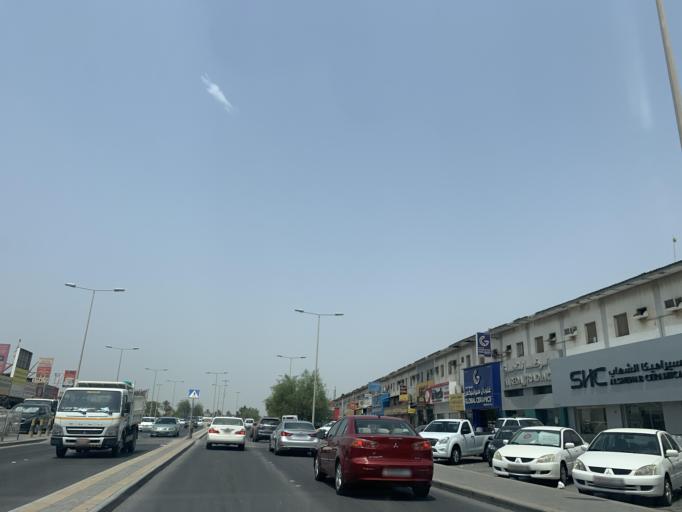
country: BH
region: Central Governorate
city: Madinat Hamad
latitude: 26.1425
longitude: 50.4915
